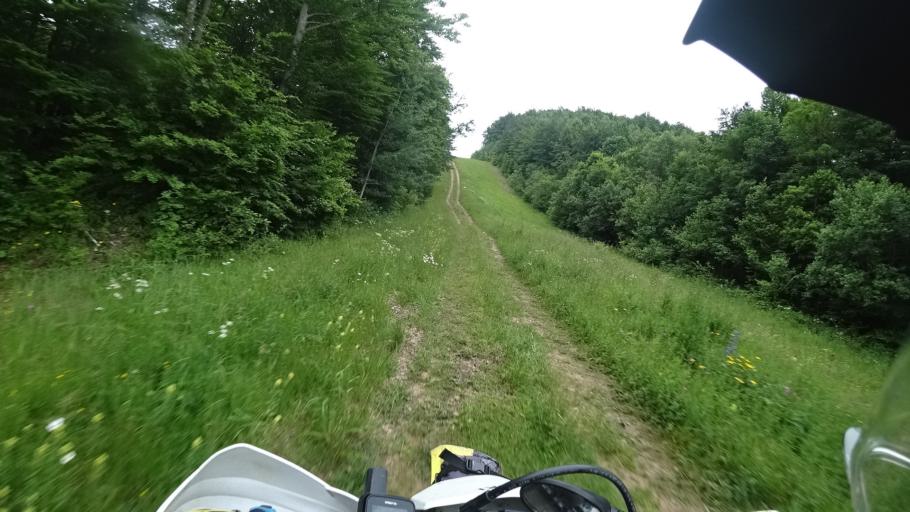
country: HR
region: Primorsko-Goranska
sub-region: Grad Delnice
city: Delnice
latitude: 45.3824
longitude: 14.8577
